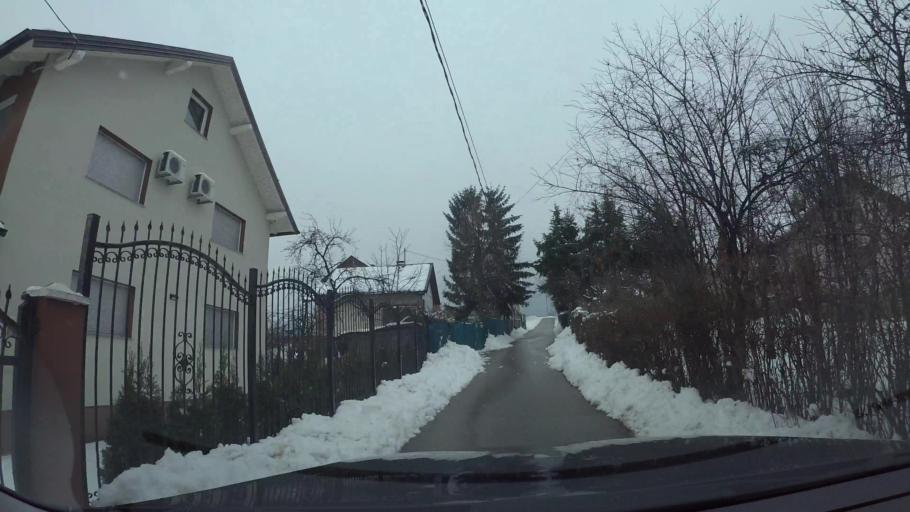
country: BA
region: Federation of Bosnia and Herzegovina
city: Hadzici
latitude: 43.8421
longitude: 18.2667
